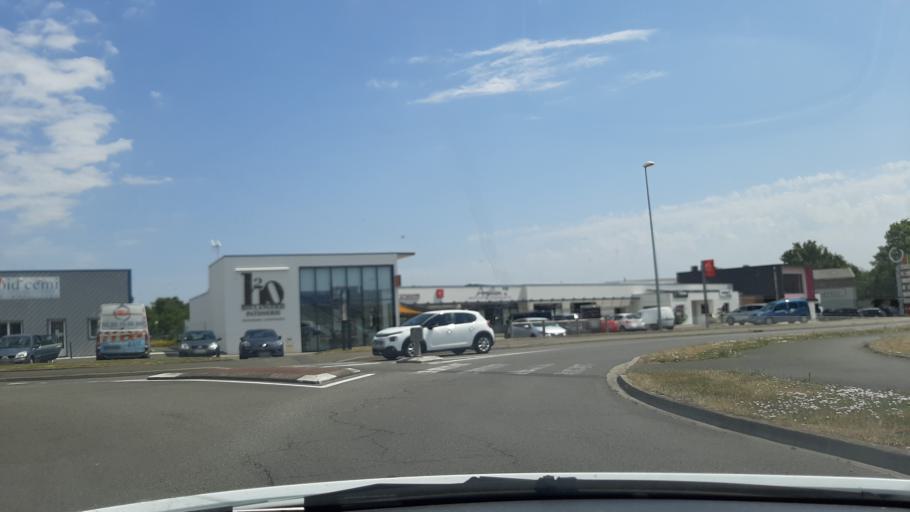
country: FR
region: Pays de la Loire
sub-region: Departement de la Vendee
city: Le Poire-sur-Vie
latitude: 46.7639
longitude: -1.4946
